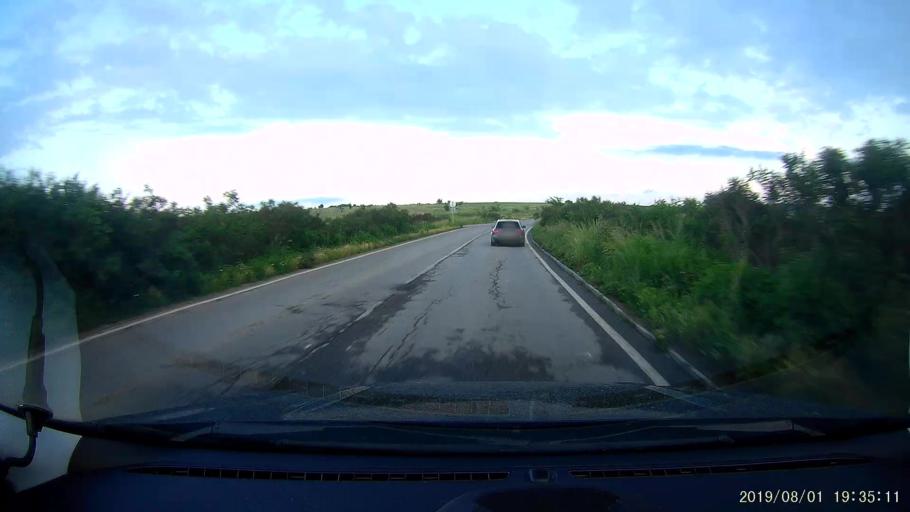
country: BG
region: Burgas
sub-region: Obshtina Sungurlare
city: Sungurlare
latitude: 42.7637
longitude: 26.8829
